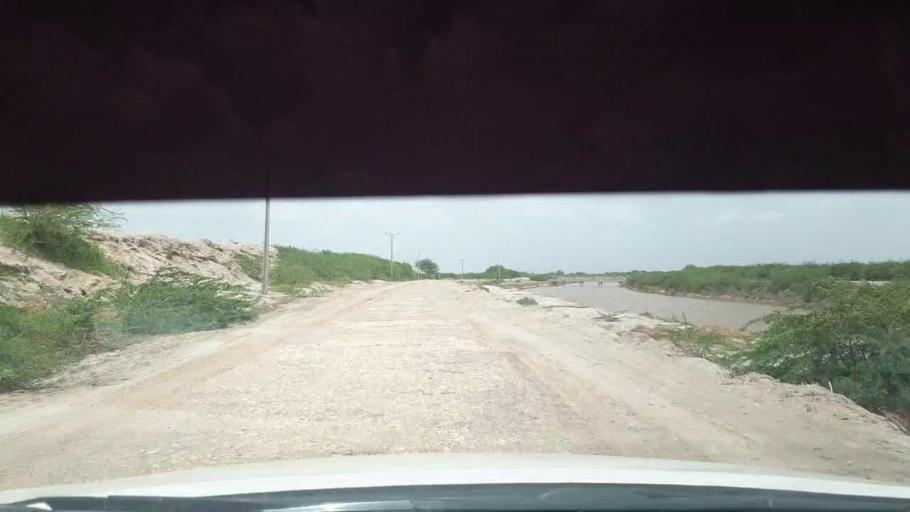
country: PK
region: Sindh
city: Kadhan
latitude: 24.5233
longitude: 69.1226
